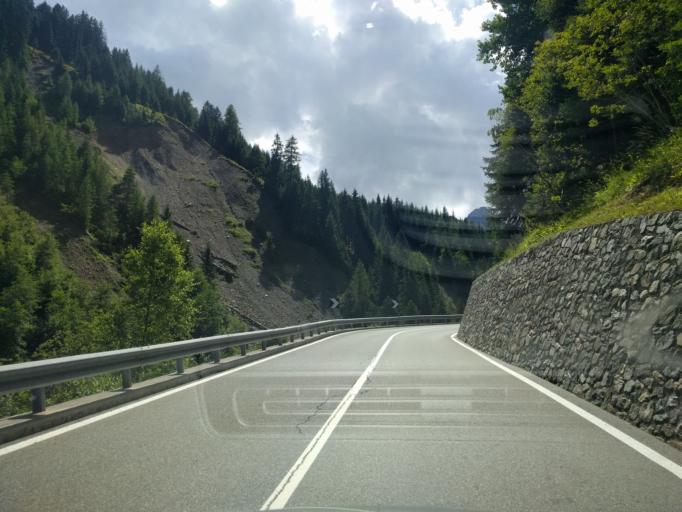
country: IT
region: Trentino-Alto Adige
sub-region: Bolzano
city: Stelvio
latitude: 46.5626
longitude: 10.5184
